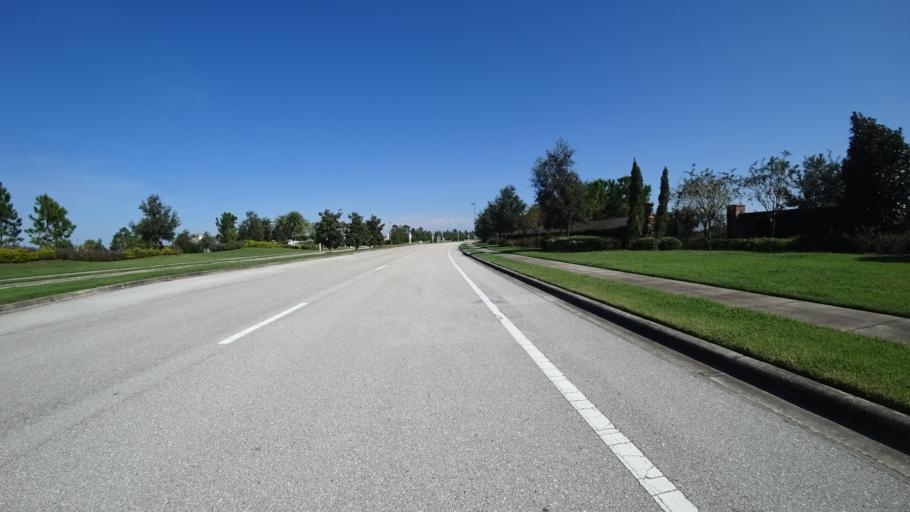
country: US
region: Florida
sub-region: Sarasota County
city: The Meadows
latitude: 27.4024
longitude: -82.3763
